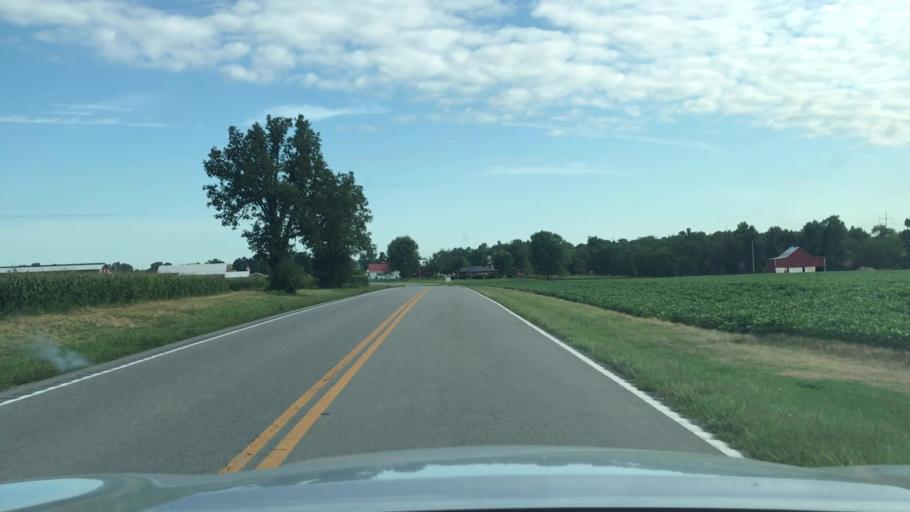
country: US
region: Kentucky
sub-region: Todd County
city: Elkton
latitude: 36.8566
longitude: -87.1588
